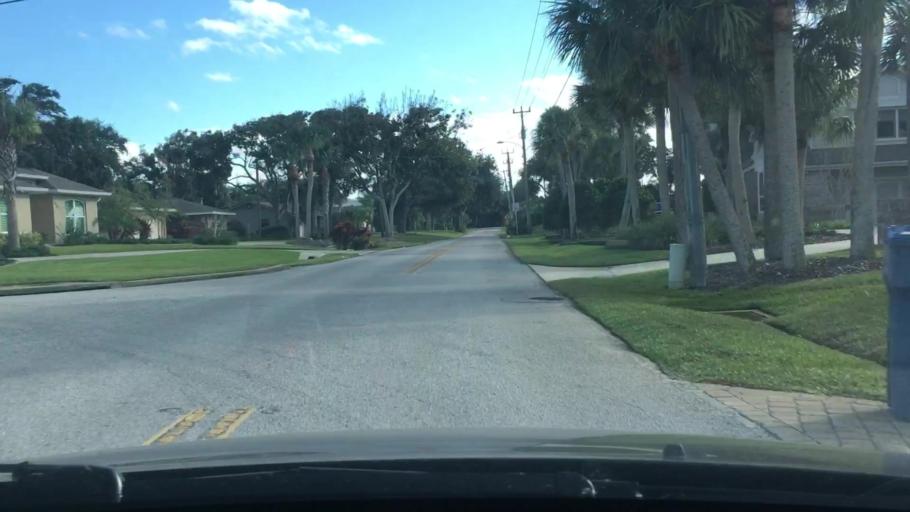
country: US
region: Florida
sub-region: Volusia County
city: Ormond-by-the-Sea
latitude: 29.3653
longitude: -81.0804
